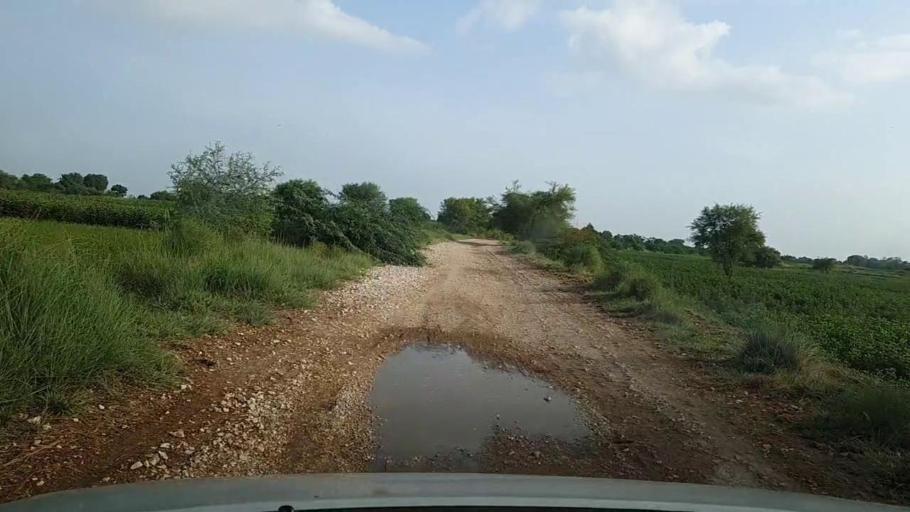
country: PK
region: Sindh
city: Pad Idan
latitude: 26.7846
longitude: 68.2207
